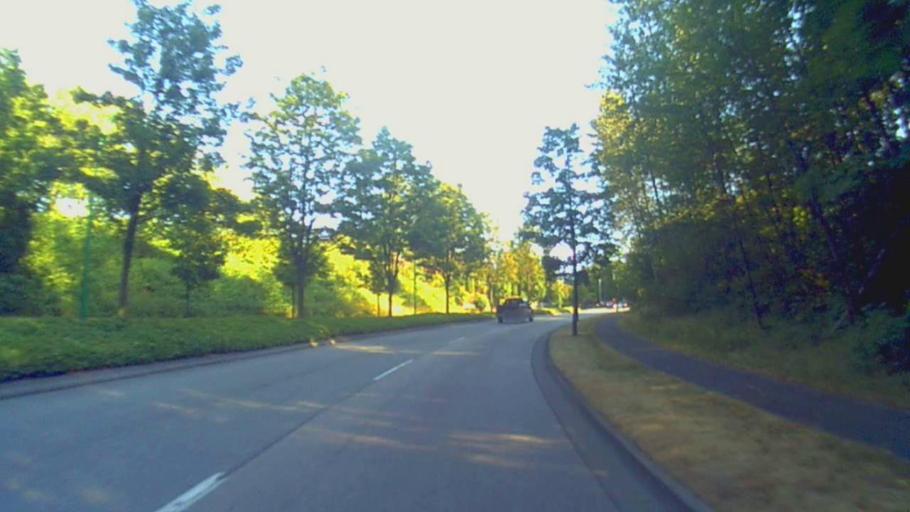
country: CA
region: British Columbia
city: New Westminster
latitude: 49.2403
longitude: -122.9068
